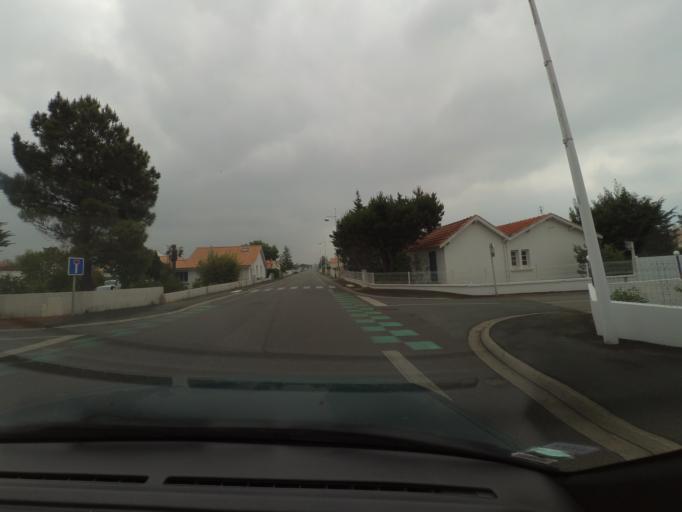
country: FR
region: Pays de la Loire
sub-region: Departement de la Vendee
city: Angles
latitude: 46.3360
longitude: -1.3292
